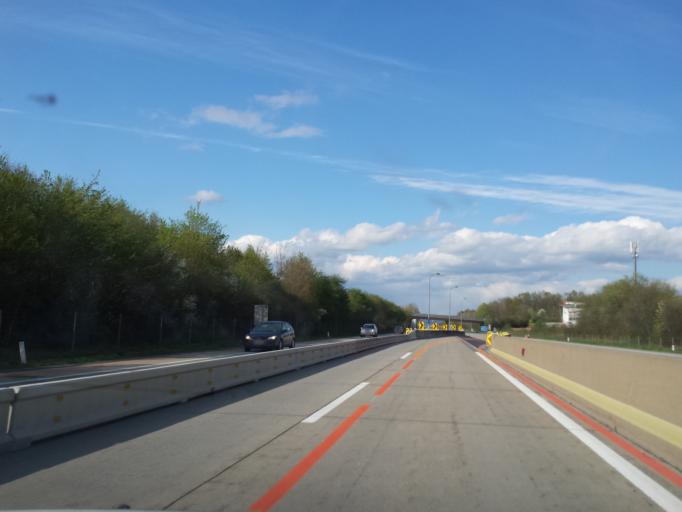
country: AT
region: Styria
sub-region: Politischer Bezirk Graz-Umgebung
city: Unterpremstatten
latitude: 46.9716
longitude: 15.3890
